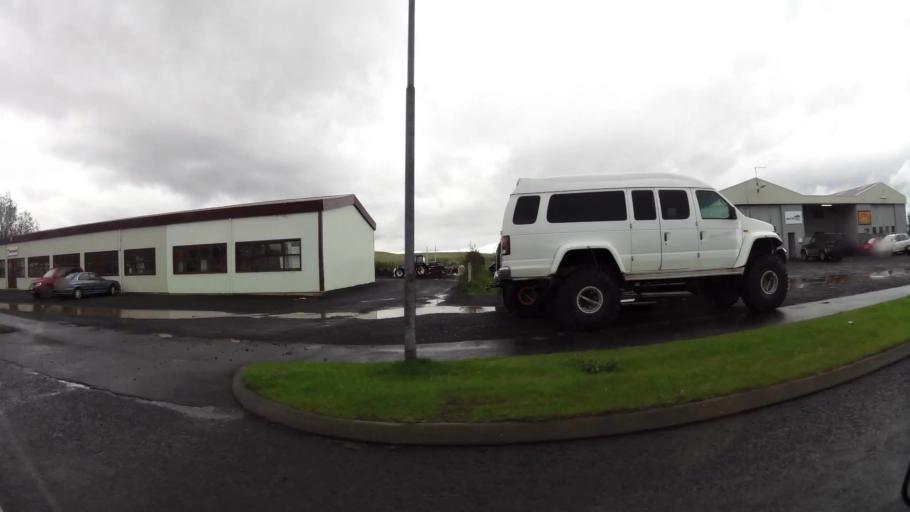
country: IS
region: South
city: Vestmannaeyjar
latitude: 63.7504
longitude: -20.2232
